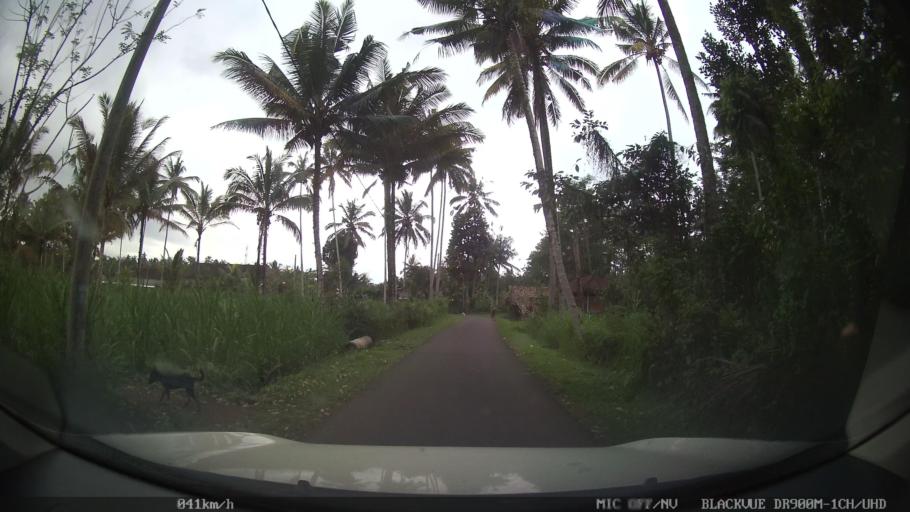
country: ID
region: Bali
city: Banjar Wangsian
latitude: -8.4340
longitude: 115.4259
